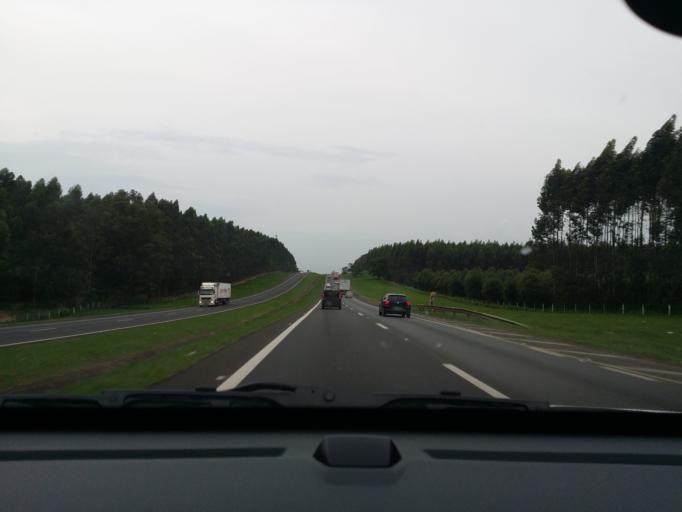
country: BR
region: Sao Paulo
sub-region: Itirapina
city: Itirapina
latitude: -22.2335
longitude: -47.7349
